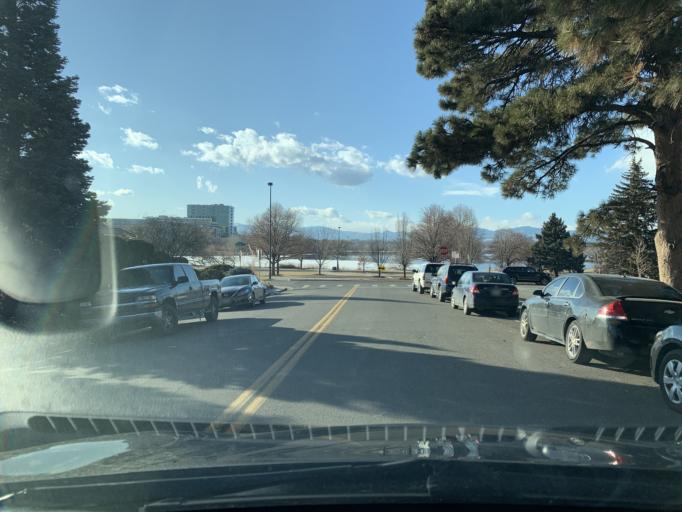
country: US
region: Colorado
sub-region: Jefferson County
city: Edgewater
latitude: 39.7452
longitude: -105.0351
